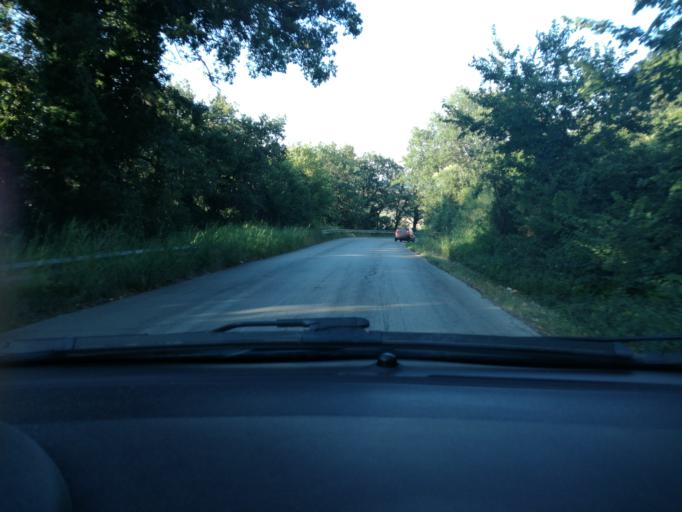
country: IT
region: Molise
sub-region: Provincia di Campobasso
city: Guglionesi
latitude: 41.9288
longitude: 14.9268
